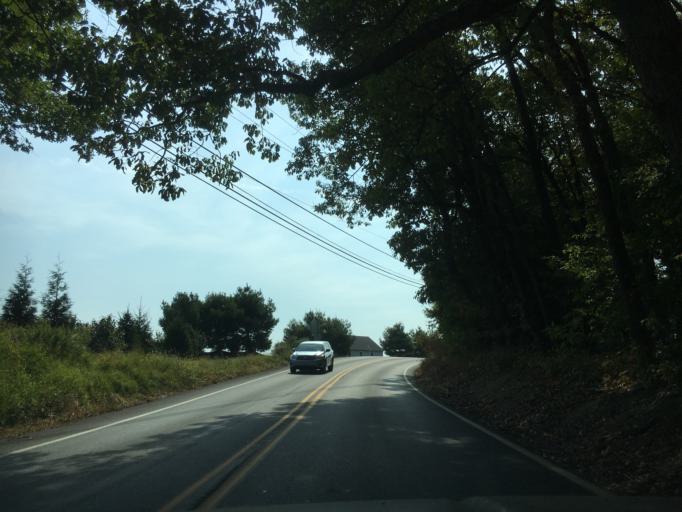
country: US
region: Pennsylvania
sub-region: Berks County
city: Topton
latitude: 40.5771
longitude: -75.7079
